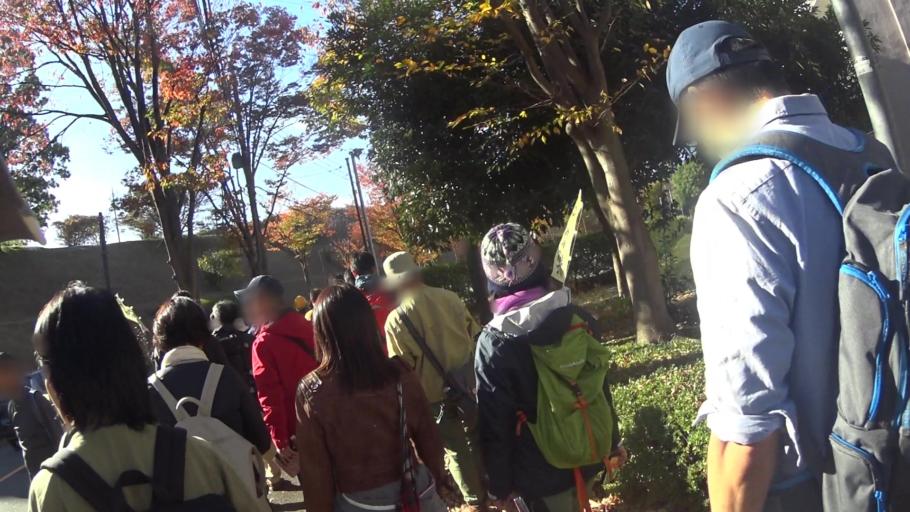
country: JP
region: Tokyo
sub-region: Machida-shi
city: Machida
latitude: 35.6087
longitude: 139.4842
